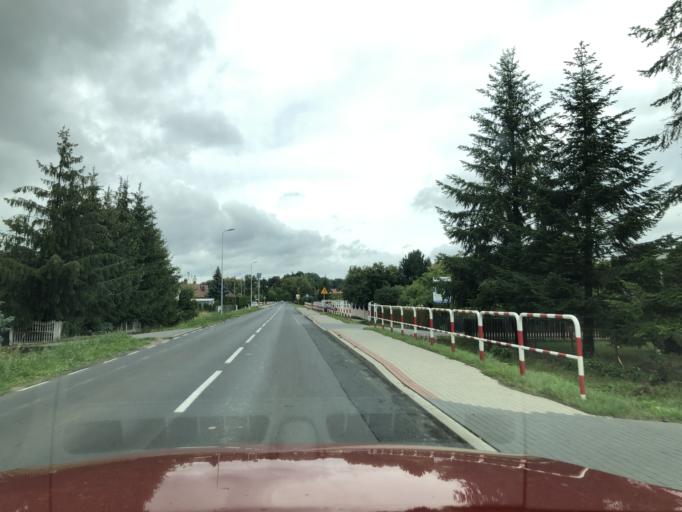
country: PL
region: Greater Poland Voivodeship
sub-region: Powiat szamotulski
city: Wronki
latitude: 52.6869
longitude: 16.3900
